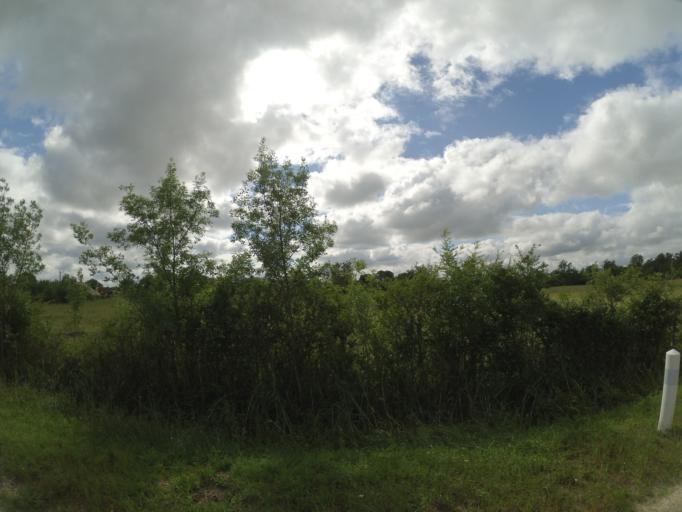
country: FR
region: Aquitaine
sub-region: Departement de la Gironde
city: Ludon-Medoc
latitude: 44.9863
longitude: -0.5771
